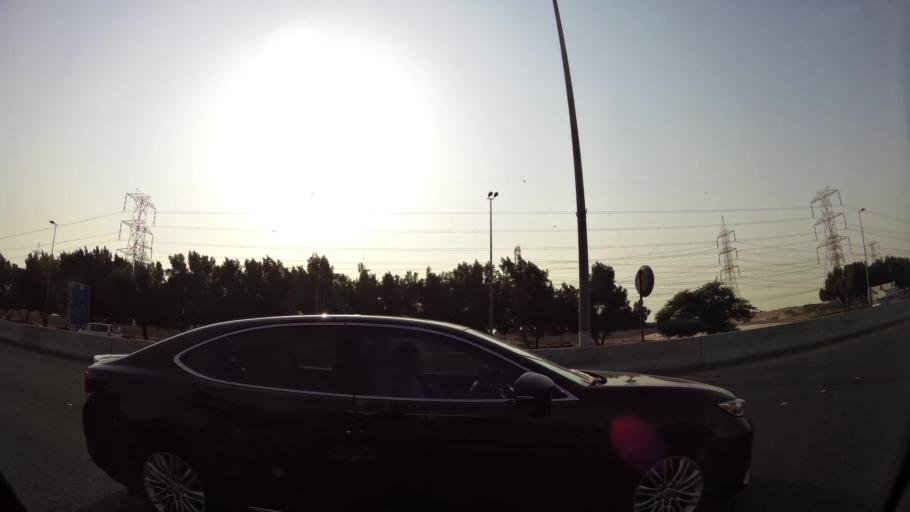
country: KW
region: Mubarak al Kabir
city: Sabah as Salim
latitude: 29.2528
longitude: 48.0464
